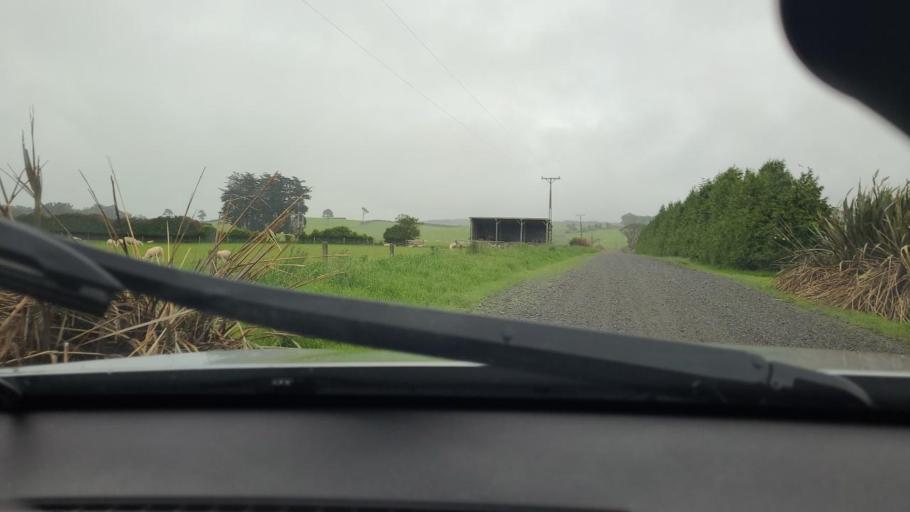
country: NZ
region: Southland
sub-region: Southland District
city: Riverton
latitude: -46.2142
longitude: 168.0472
